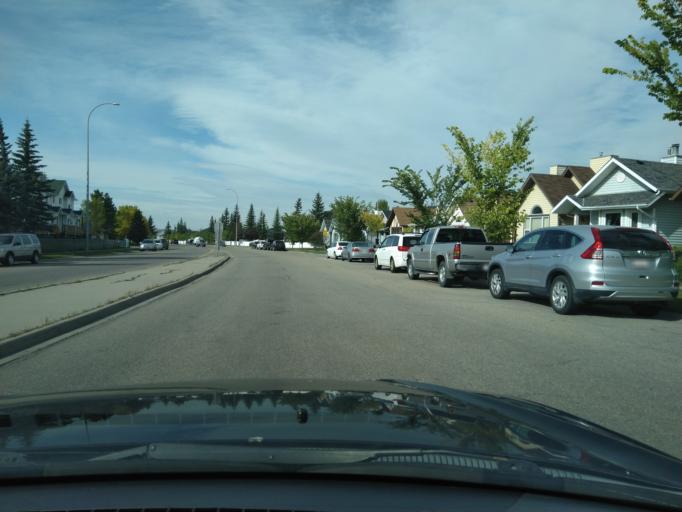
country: CA
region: Alberta
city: Calgary
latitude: 51.1371
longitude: -114.0910
